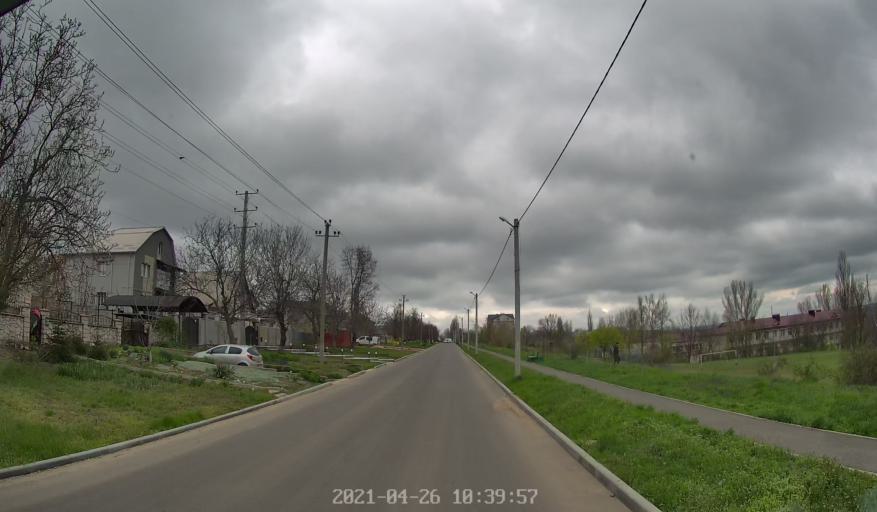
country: MD
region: Chisinau
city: Cricova
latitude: 47.1321
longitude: 28.8610
